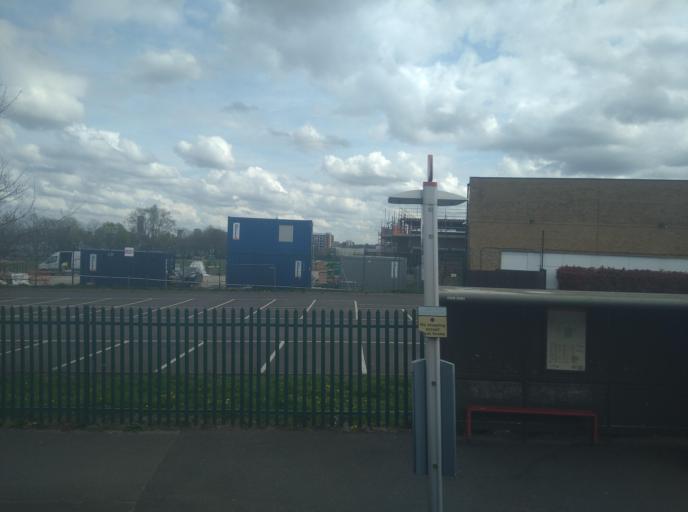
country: GB
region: England
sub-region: Greater London
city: Purley
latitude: 51.3592
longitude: -0.1292
